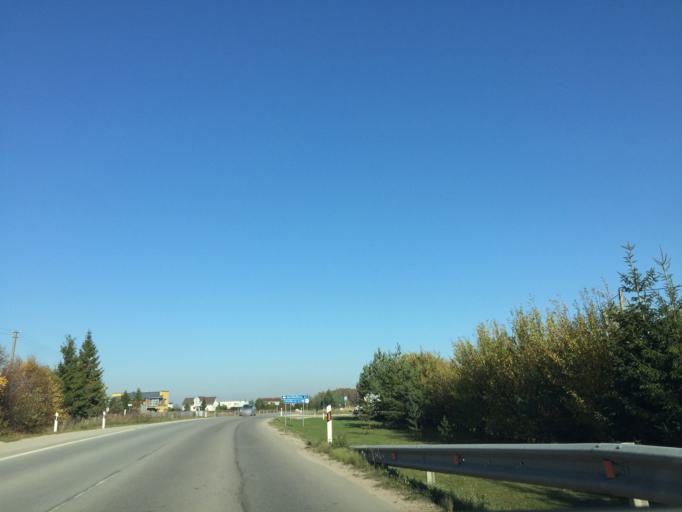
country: LT
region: Klaipedos apskritis
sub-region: Klaipeda
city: Klaipeda
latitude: 55.7549
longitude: 21.1927
